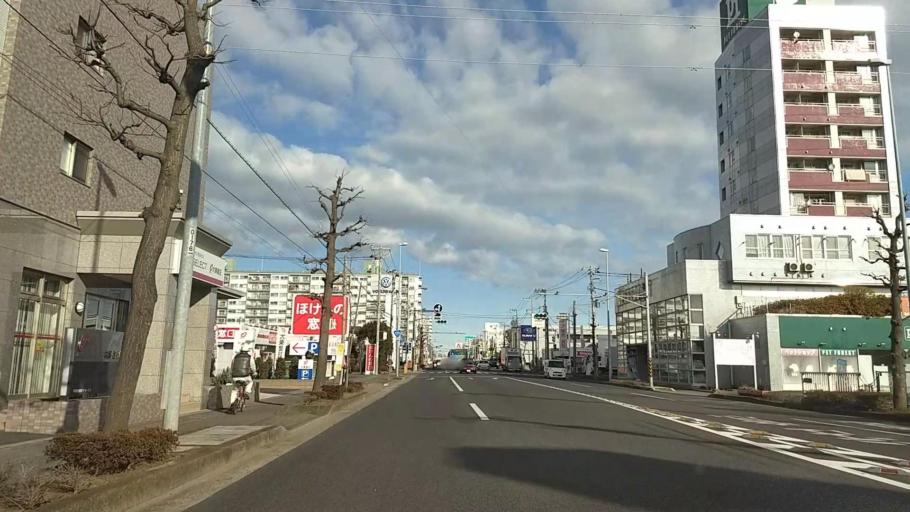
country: JP
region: Kanagawa
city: Hiratsuka
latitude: 35.3672
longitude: 139.3615
